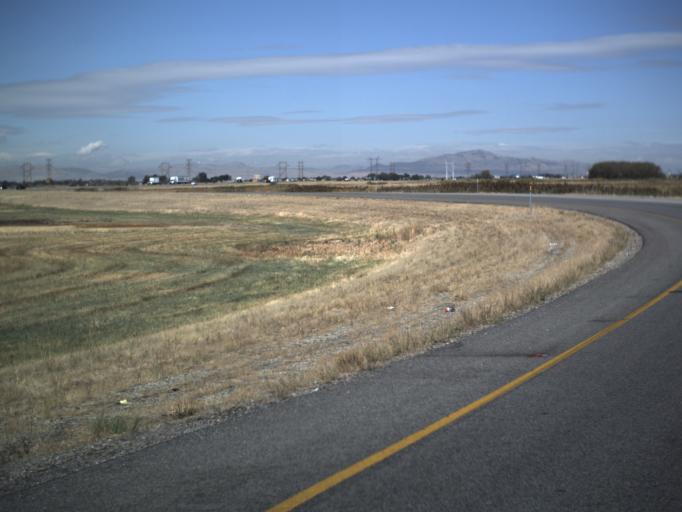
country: US
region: Utah
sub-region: Box Elder County
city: Brigham City
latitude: 41.5102
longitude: -112.0573
